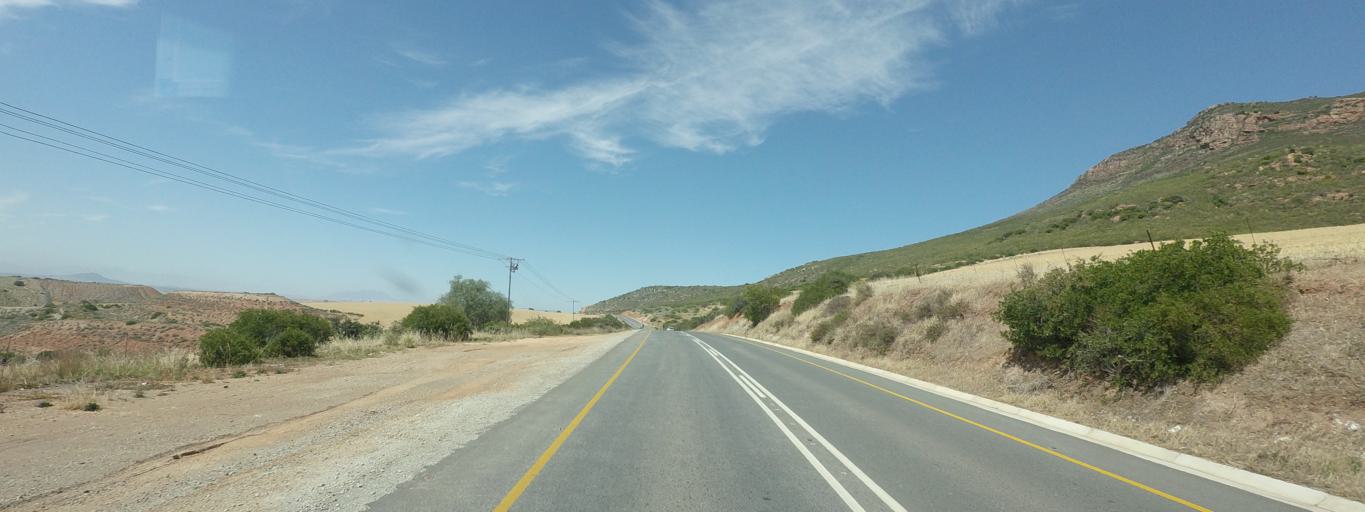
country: ZA
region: Western Cape
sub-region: West Coast District Municipality
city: Piketberg
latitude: -32.9239
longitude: 18.7567
